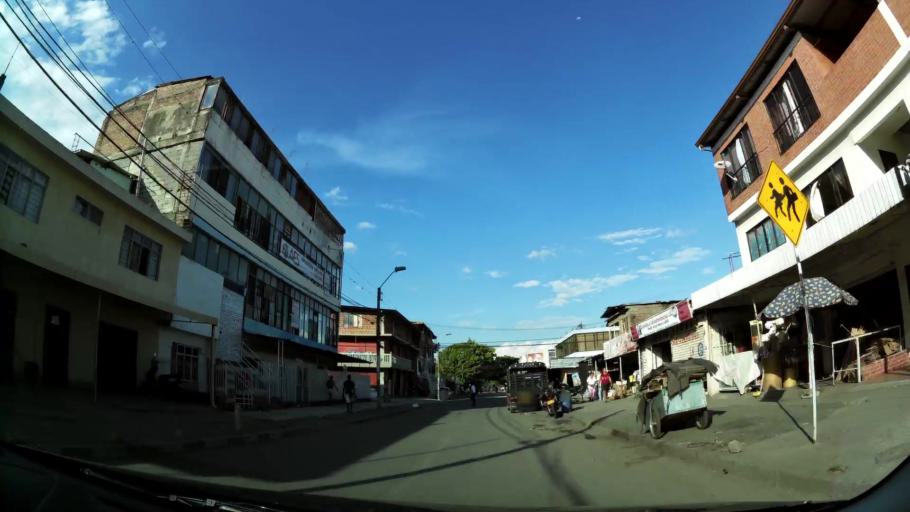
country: CO
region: Valle del Cauca
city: Cali
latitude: 3.4067
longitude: -76.5083
